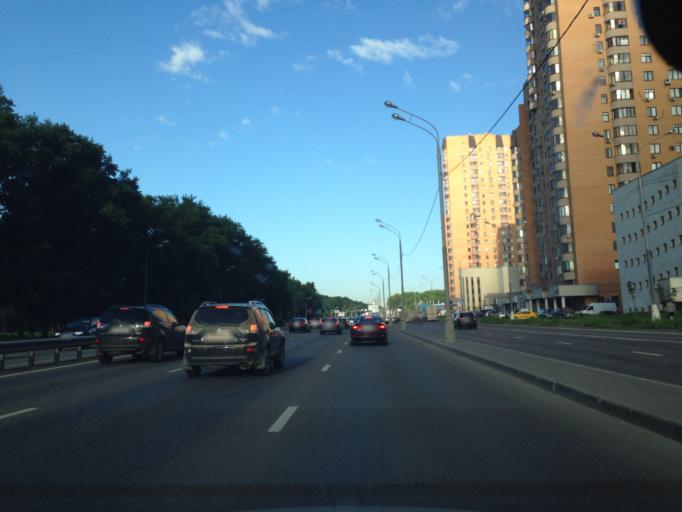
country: RU
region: Moscow
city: Ivanovskoye
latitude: 55.7738
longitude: 37.8286
